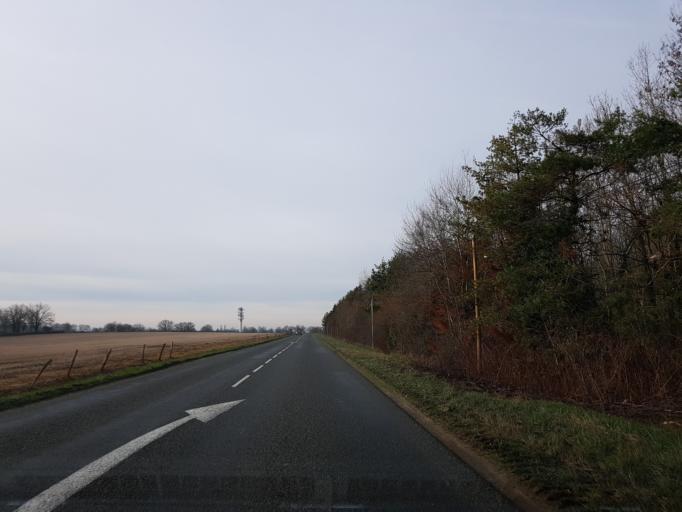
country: FR
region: Auvergne
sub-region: Departement de l'Allier
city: Yzeure
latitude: 46.5787
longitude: 3.3989
